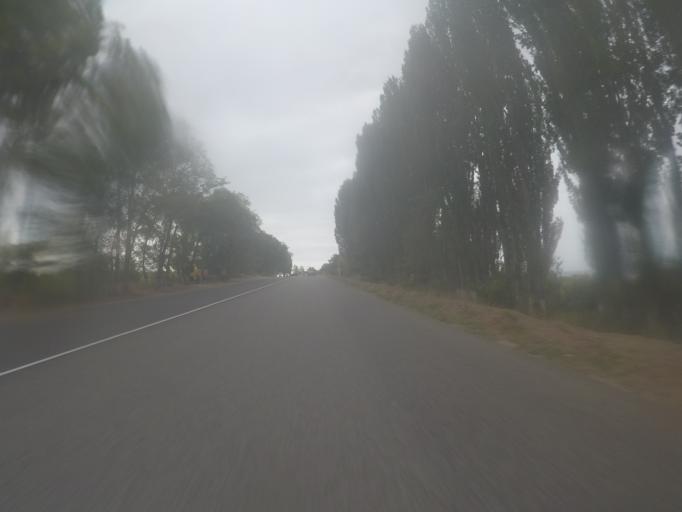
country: KG
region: Ysyk-Koel
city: Cholpon-Ata
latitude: 42.6689
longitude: 77.2828
